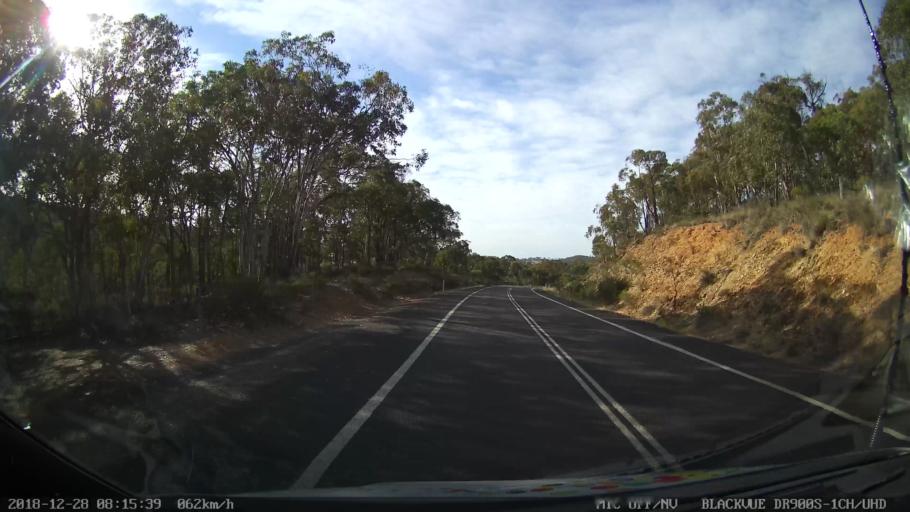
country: AU
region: New South Wales
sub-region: Blayney
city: Blayney
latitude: -33.8246
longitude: 149.3295
